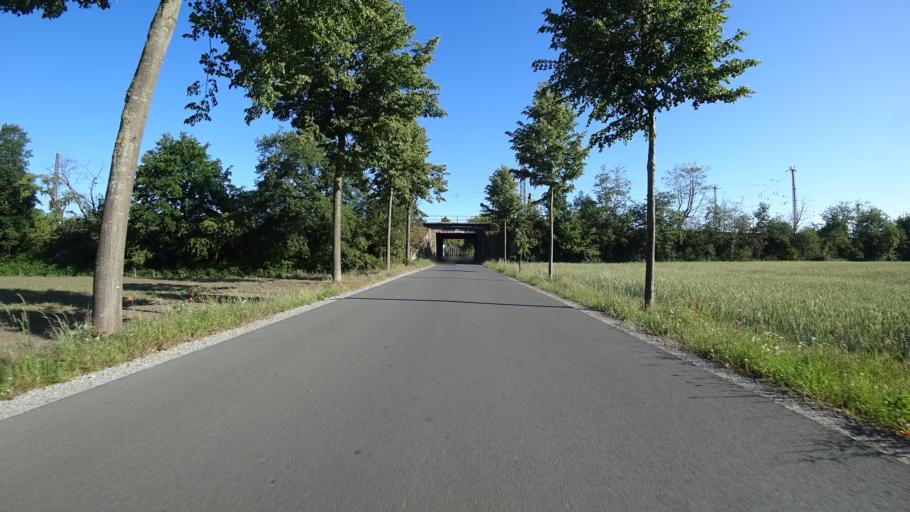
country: DE
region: North Rhine-Westphalia
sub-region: Regierungsbezirk Detmold
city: Rheda-Wiedenbruck
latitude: 51.8603
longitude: 8.3068
